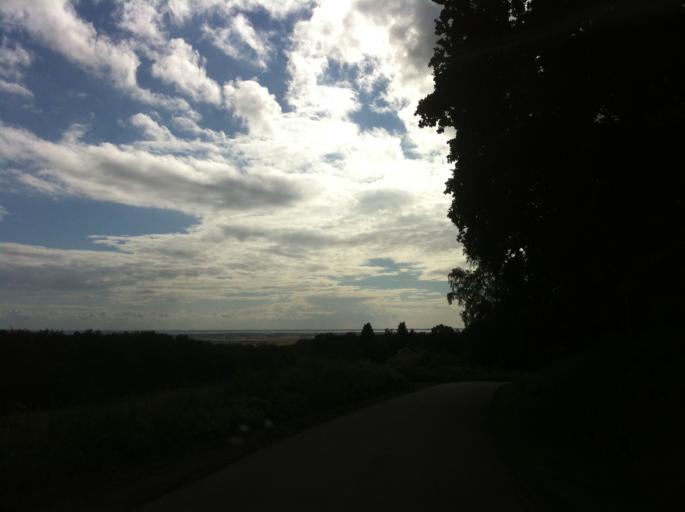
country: SE
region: Skane
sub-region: Bastads Kommun
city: Bastad
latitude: 56.4018
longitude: 12.9058
